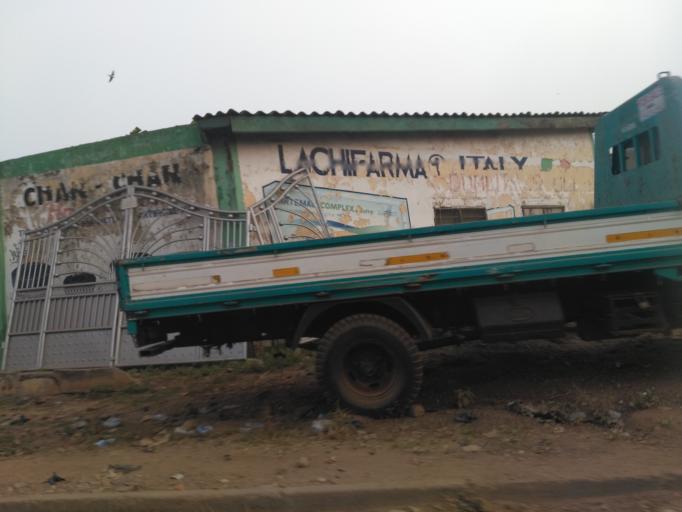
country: GH
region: Ashanti
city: Kumasi
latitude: 6.6813
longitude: -1.6156
